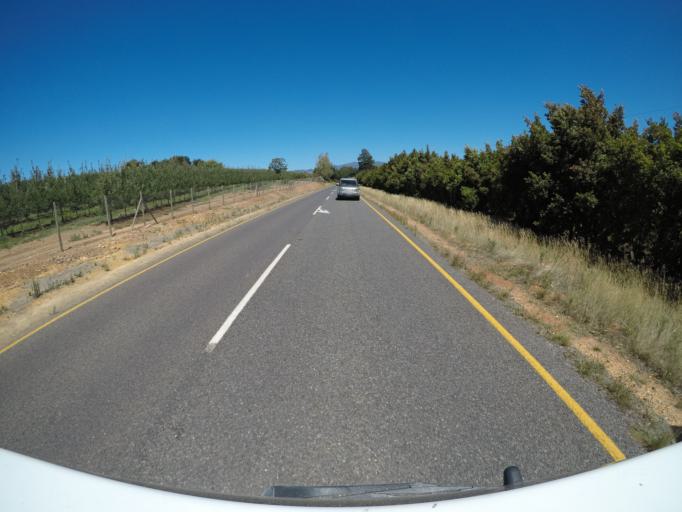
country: ZA
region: Western Cape
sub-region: Overberg District Municipality
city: Grabouw
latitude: -34.2107
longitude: 19.0489
